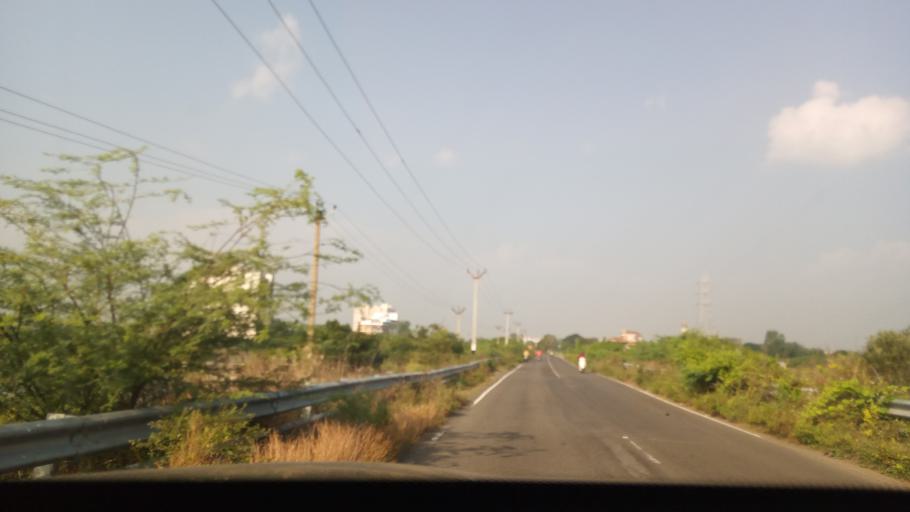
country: IN
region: Tamil Nadu
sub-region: Kancheepuram
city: Vengavasal
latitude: 12.7839
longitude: 80.2341
